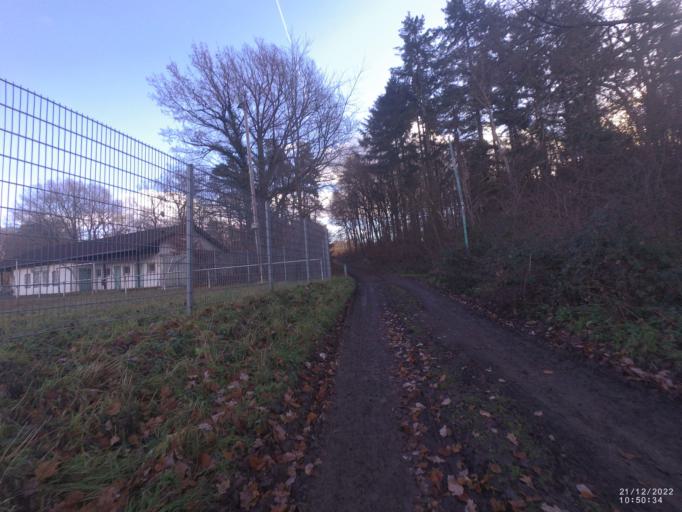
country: DE
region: Rheinland-Pfalz
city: Konigsfeld
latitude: 50.4994
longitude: 7.1874
